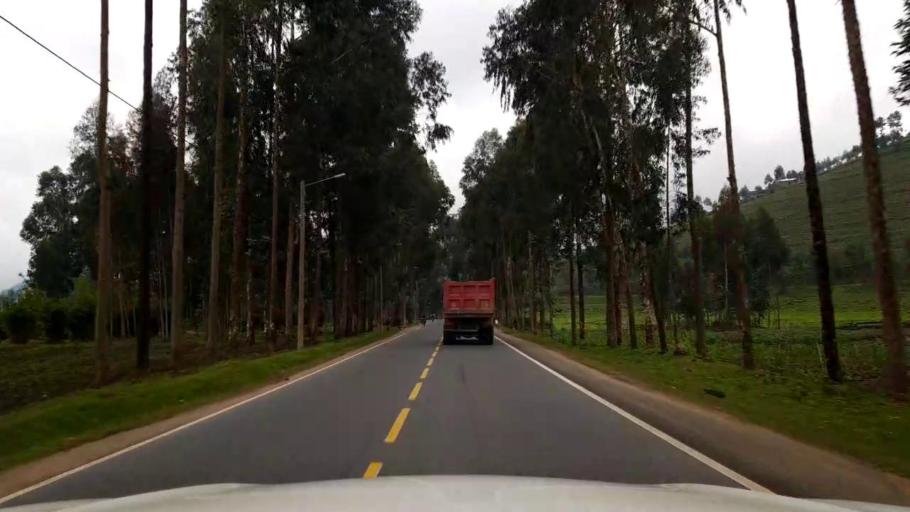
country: RW
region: Northern Province
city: Musanze
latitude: -1.5696
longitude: 29.5447
